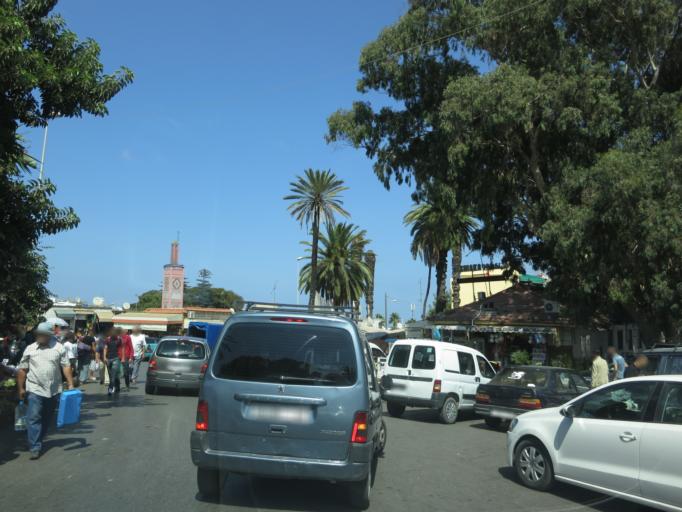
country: MA
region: Tanger-Tetouan
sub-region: Tanger-Assilah
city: Tangier
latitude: 35.7832
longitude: -5.8144
